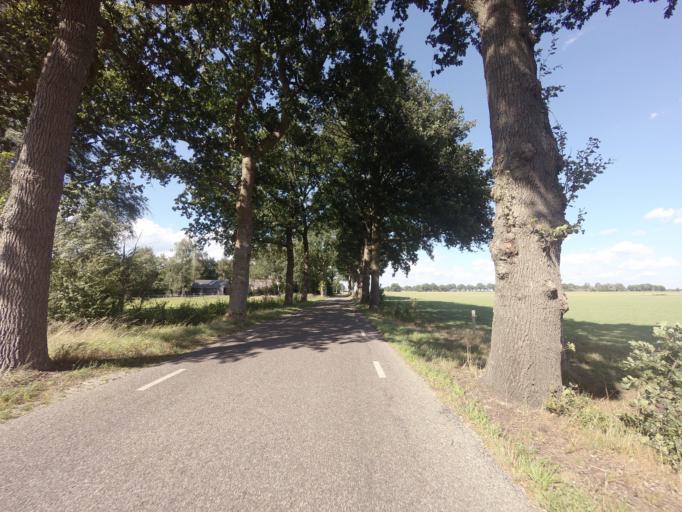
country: NL
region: Drenthe
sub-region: Gemeente Hoogeveen
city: Hoogeveen
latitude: 52.6283
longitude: 6.4834
